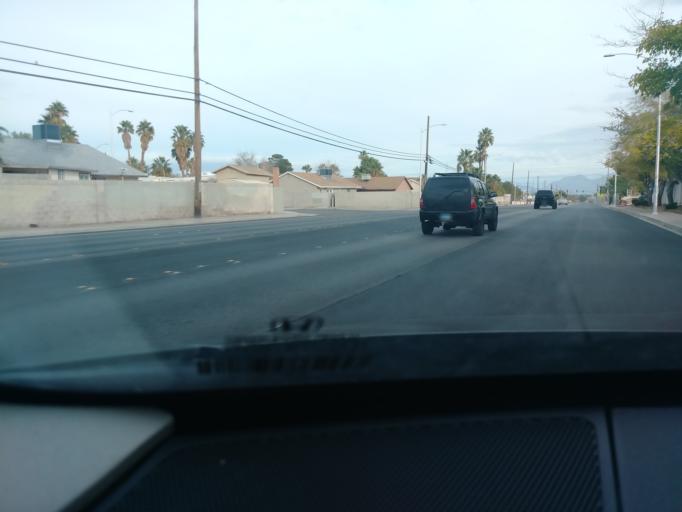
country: US
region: Nevada
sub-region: Clark County
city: Spring Valley
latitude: 36.1808
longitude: -115.2187
